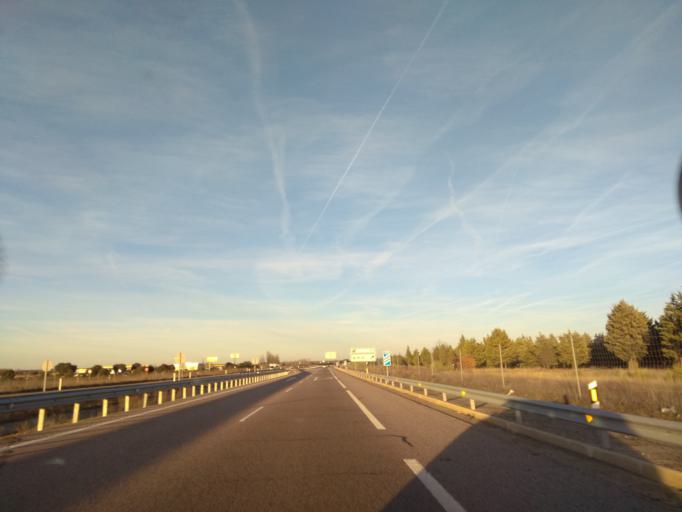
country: ES
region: Castille and Leon
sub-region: Provincia de Salamanca
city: Castraz
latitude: 40.6908
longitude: -6.4203
